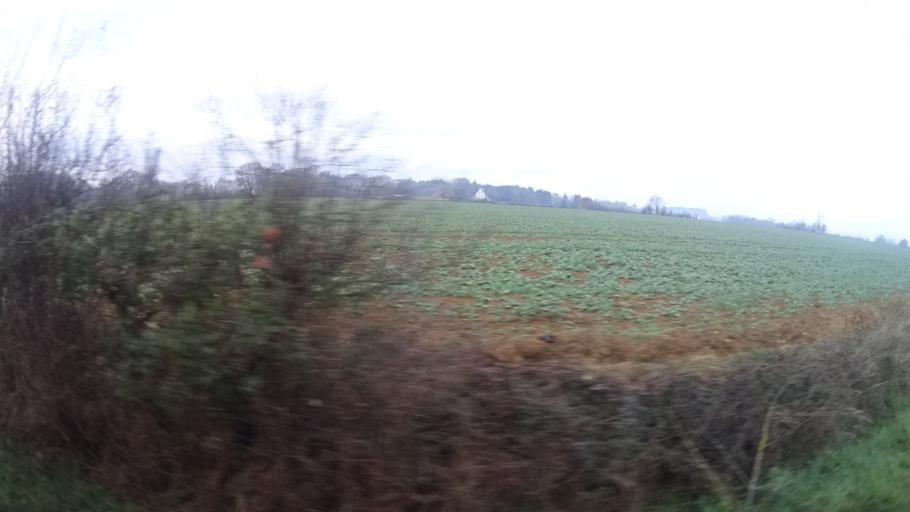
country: FR
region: Pays de la Loire
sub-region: Departement de la Loire-Atlantique
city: Avessac
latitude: 47.6473
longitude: -2.0242
